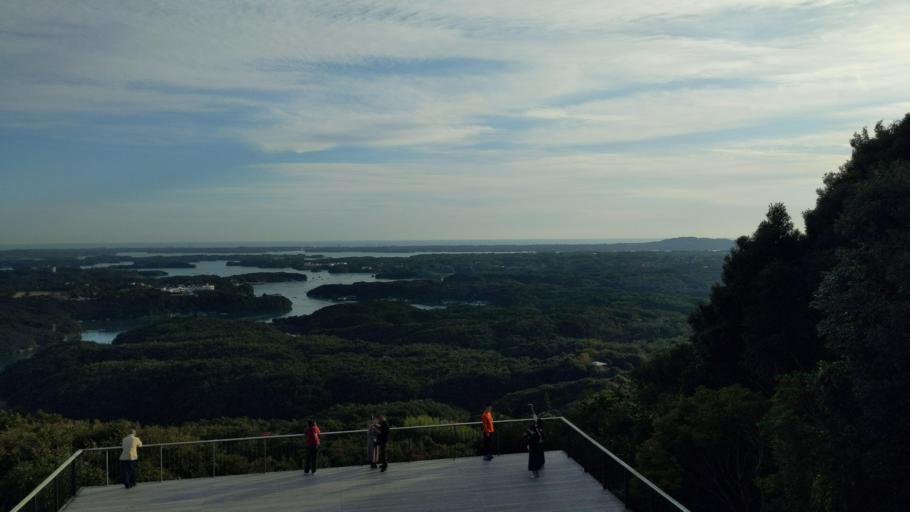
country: JP
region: Mie
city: Toba
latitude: 34.3318
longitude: 136.7991
